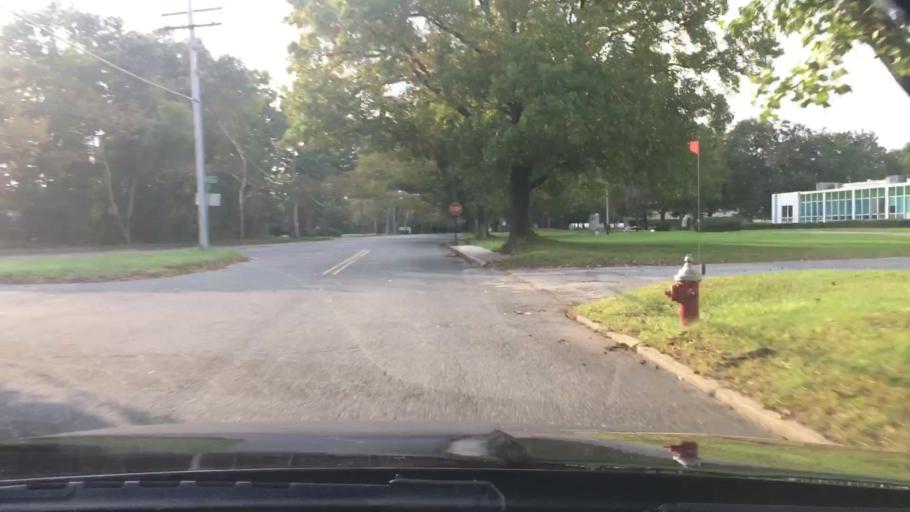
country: US
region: New York
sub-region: Suffolk County
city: Melville
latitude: 40.7684
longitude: -73.4084
